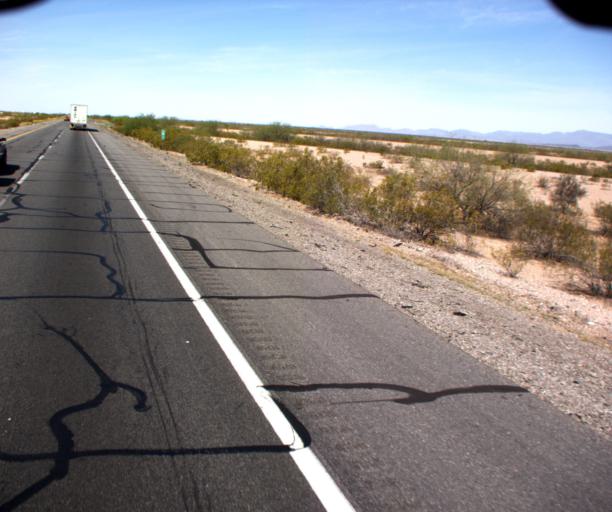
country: US
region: Arizona
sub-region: La Paz County
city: Salome
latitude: 33.5388
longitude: -113.1589
